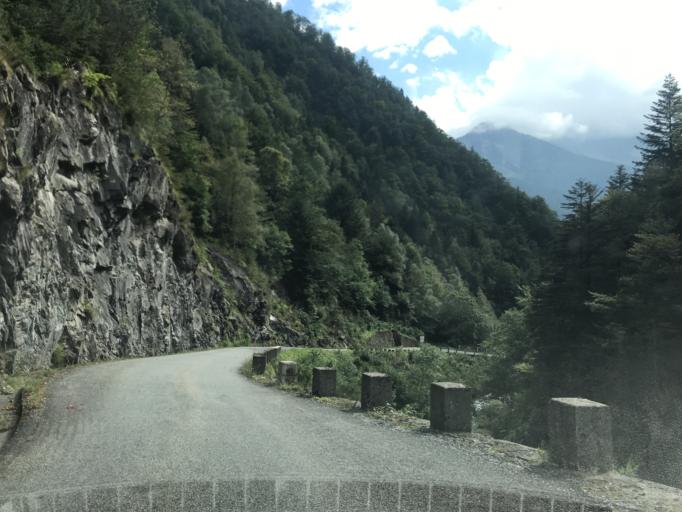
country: FR
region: Midi-Pyrenees
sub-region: Departement des Hautes-Pyrenees
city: Saint-Lary-Soulan
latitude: 42.8001
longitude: 0.2299
